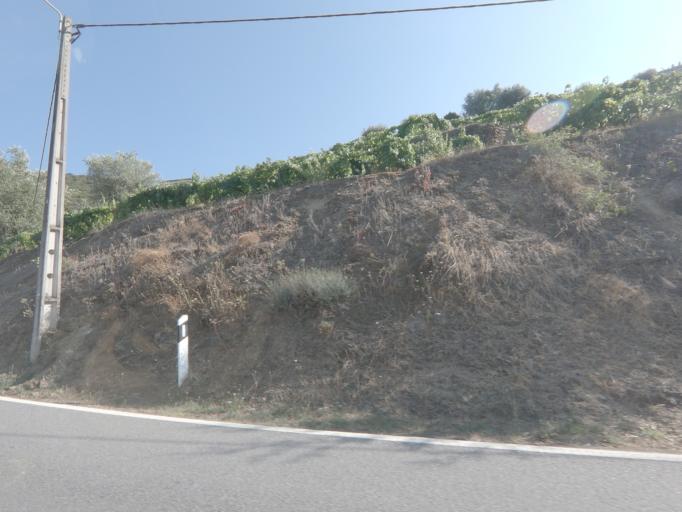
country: PT
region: Viseu
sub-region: Tabuaco
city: Tabuaco
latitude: 41.1408
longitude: -7.5730
